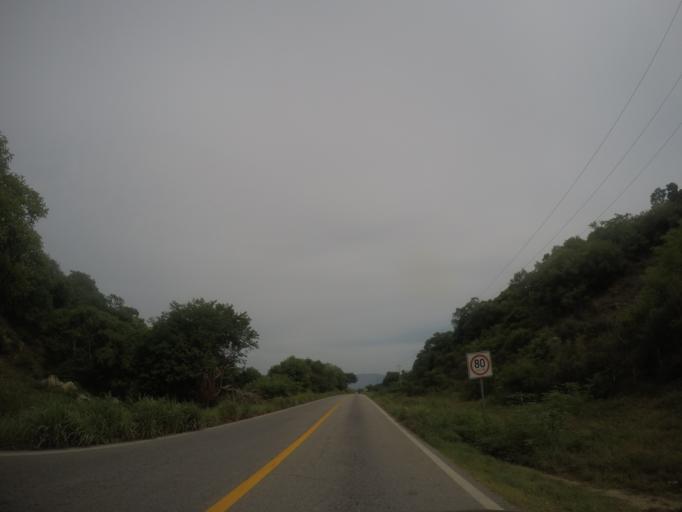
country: MX
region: Oaxaca
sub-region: Villa de Tututepec de Melchor Ocampo
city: Santa Rosa de Lima
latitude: 15.9732
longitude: -97.4007
